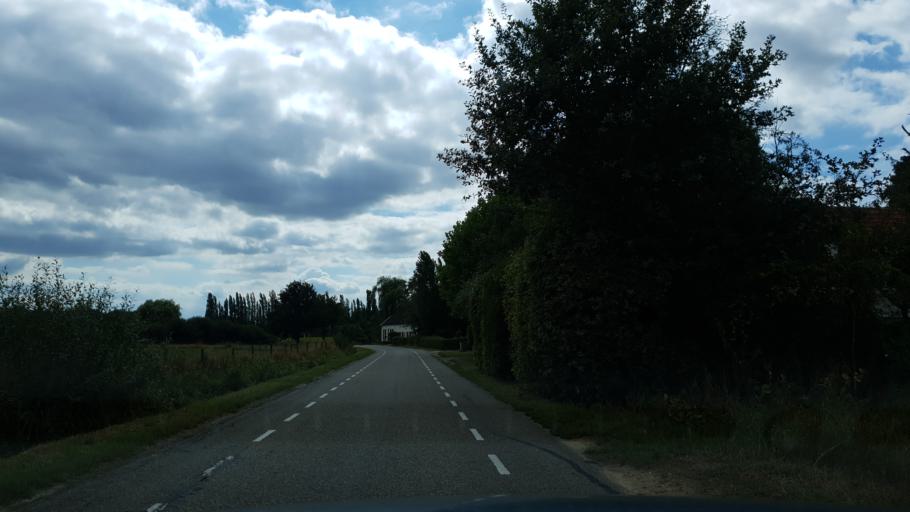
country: NL
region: North Brabant
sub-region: Gemeente Grave
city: Grave
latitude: 51.7628
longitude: 5.7973
